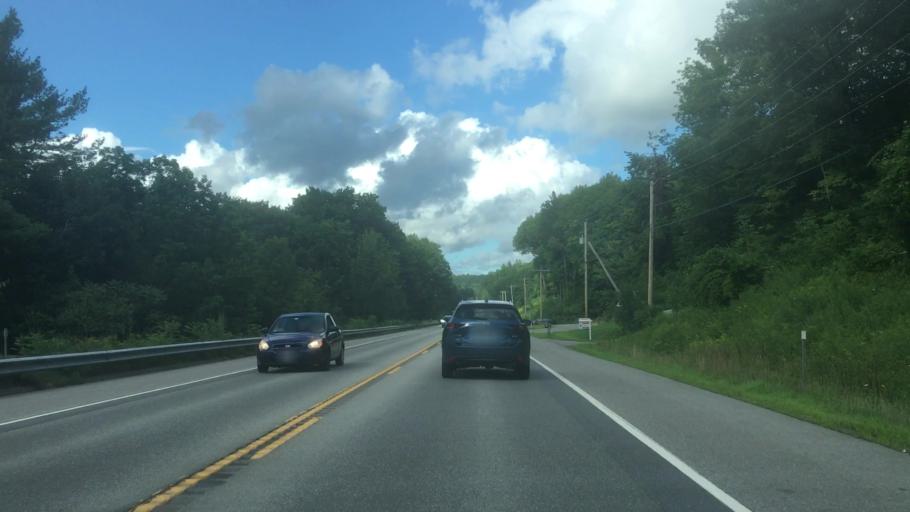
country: US
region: New Hampshire
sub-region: Cheshire County
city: Chesterfield
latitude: 42.9028
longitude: -72.4204
